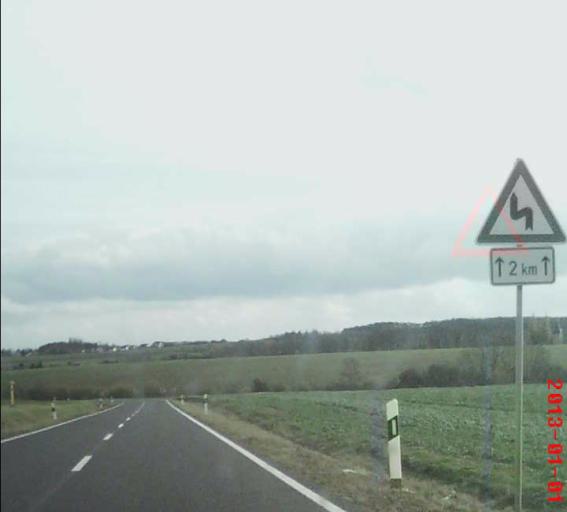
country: DE
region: Thuringia
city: Anrode
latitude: 51.2454
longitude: 10.3555
